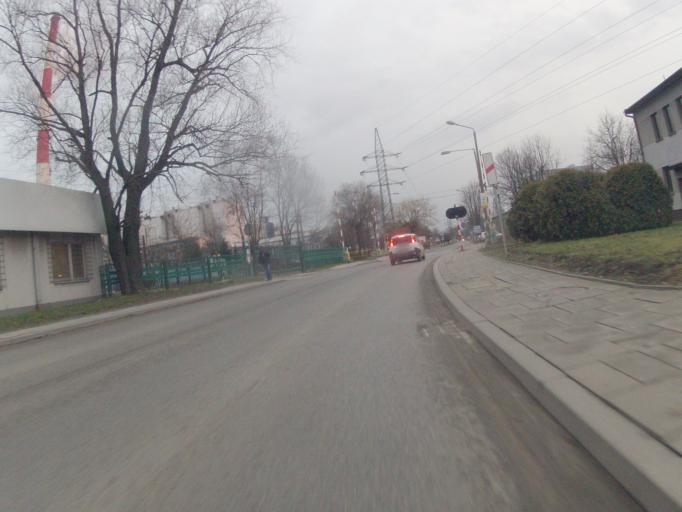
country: PL
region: Lesser Poland Voivodeship
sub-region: Krakow
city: Krakow
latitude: 50.0558
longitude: 20.0023
